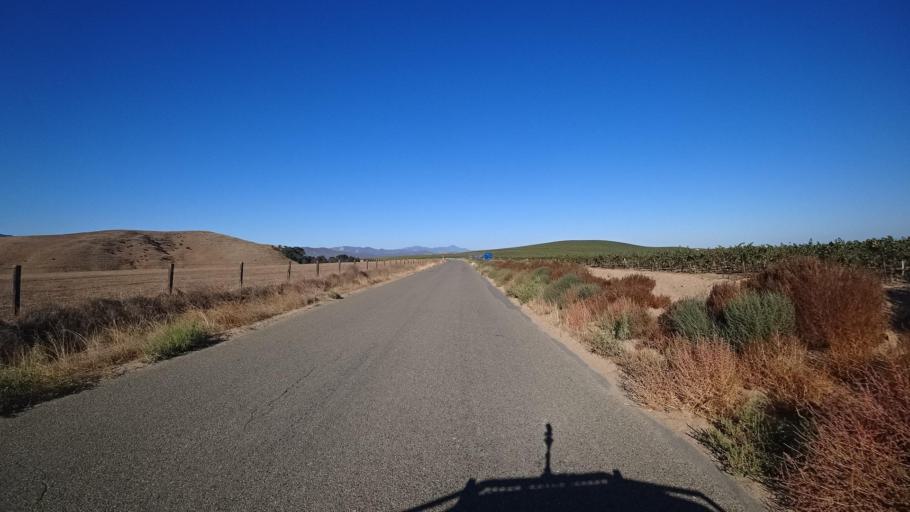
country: US
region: California
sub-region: Monterey County
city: King City
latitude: 36.1124
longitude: -121.0625
